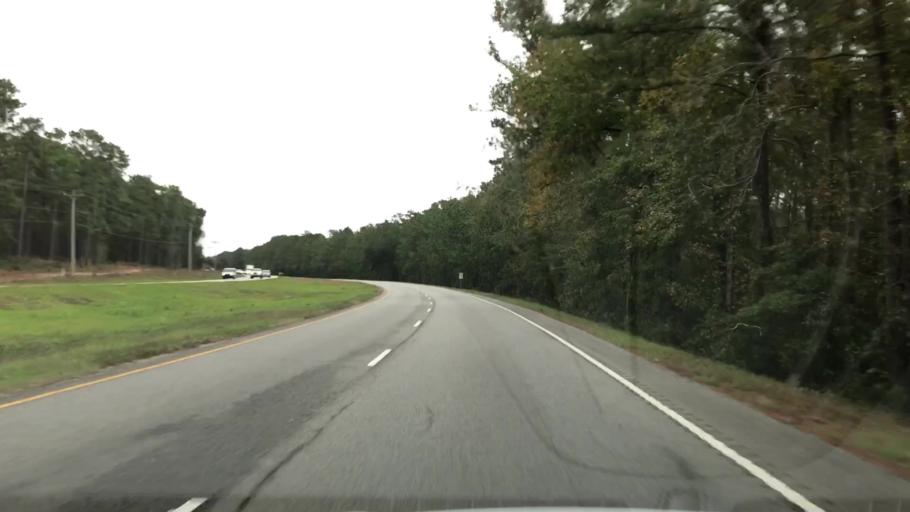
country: US
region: South Carolina
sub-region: Georgetown County
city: Georgetown
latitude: 33.3655
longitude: -79.2233
